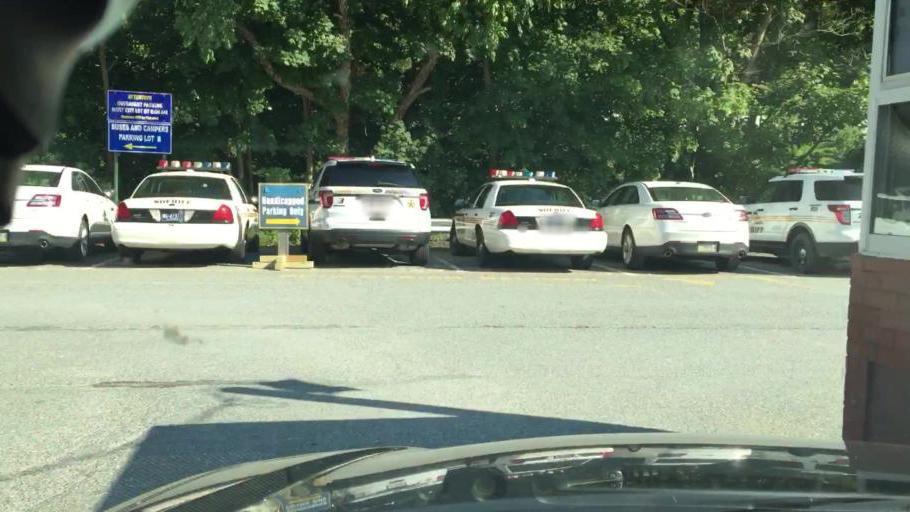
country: US
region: Pennsylvania
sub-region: Carbon County
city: Jim Thorpe
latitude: 40.8637
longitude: -75.7368
